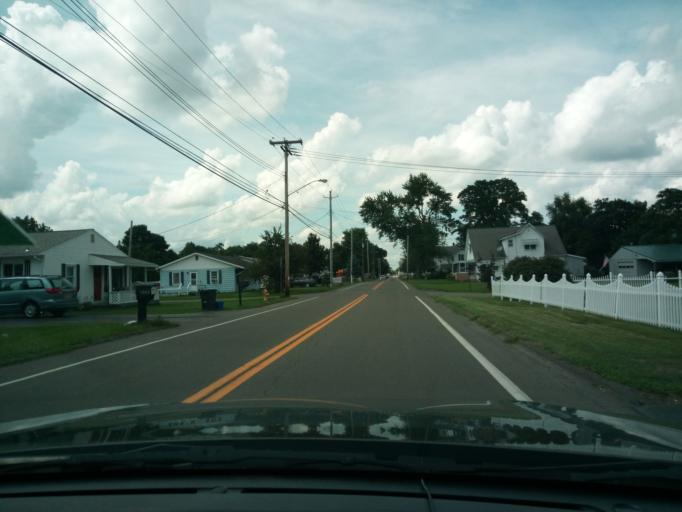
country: US
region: New York
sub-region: Chemung County
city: Southport
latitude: 42.0611
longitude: -76.7940
